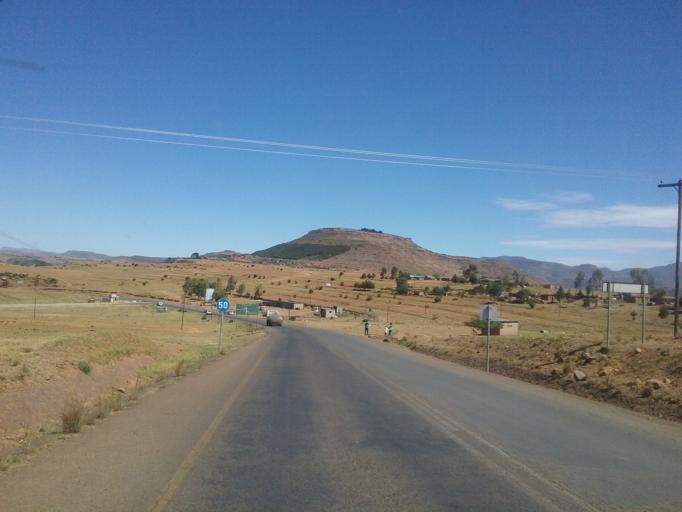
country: LS
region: Quthing
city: Quthing
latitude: -30.3901
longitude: 27.6260
